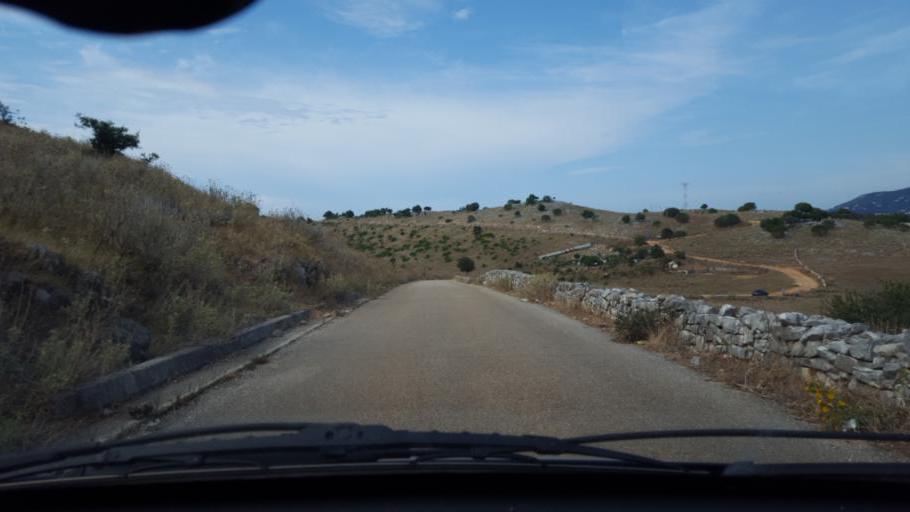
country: AL
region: Vlore
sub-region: Rrethi i Sarandes
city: Xarre
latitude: 39.7569
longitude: 19.9850
